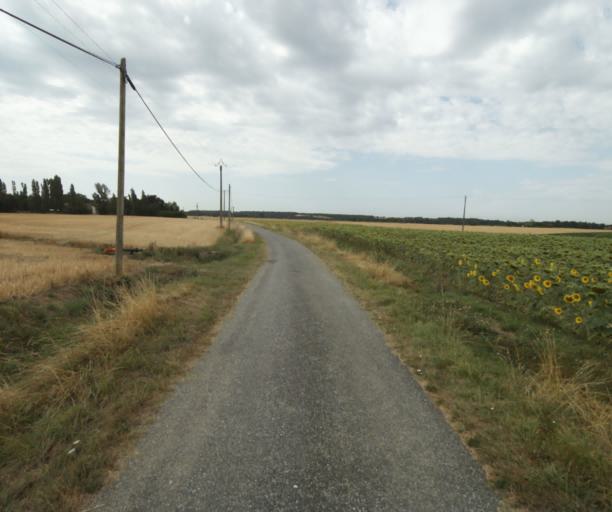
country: FR
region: Midi-Pyrenees
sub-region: Departement de la Haute-Garonne
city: Saint-Felix-Lauragais
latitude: 43.4447
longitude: 1.9362
